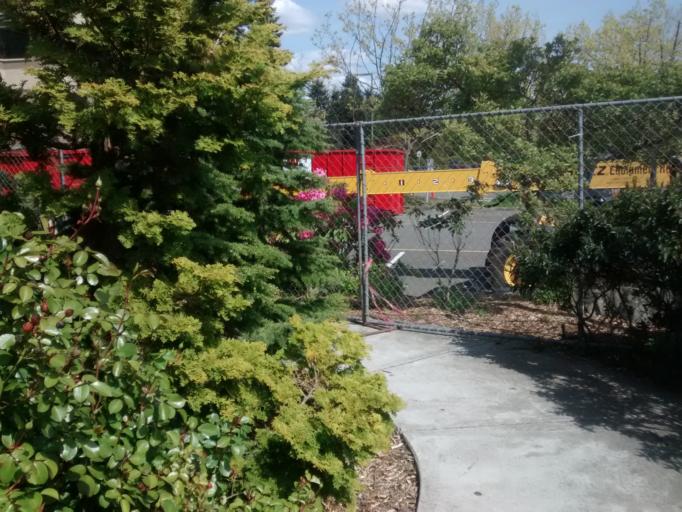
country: US
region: Washington
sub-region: Snohomish County
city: Lynnwood
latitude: 47.8147
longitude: -122.3275
